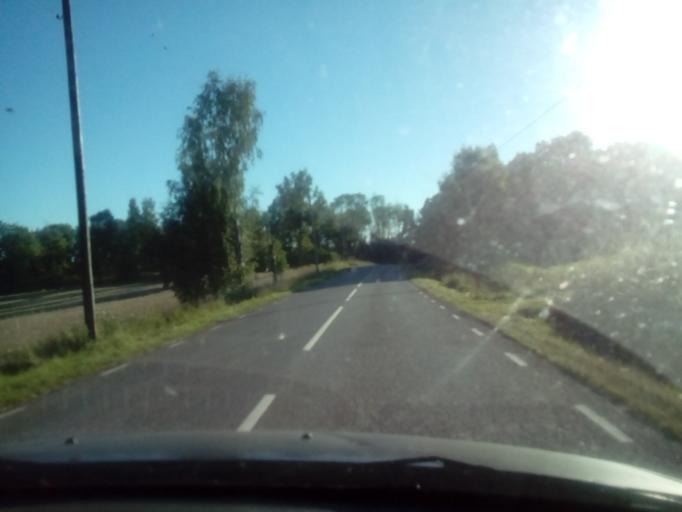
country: SE
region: Kalmar
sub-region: Vasterviks Kommun
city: Ankarsrum
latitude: 57.7817
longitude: 16.2866
